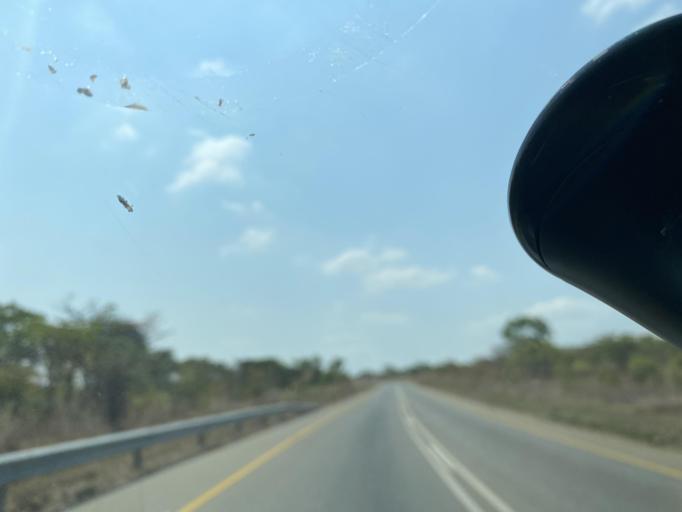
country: ZM
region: Lusaka
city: Chongwe
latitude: -15.5338
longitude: 28.6397
